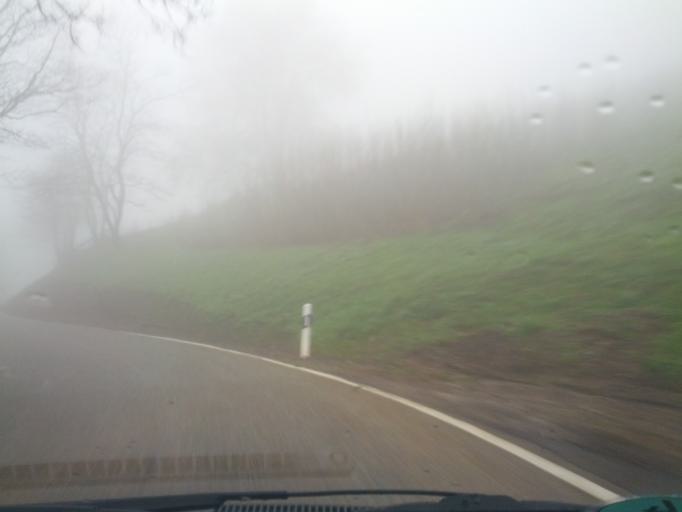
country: DE
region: Baden-Wuerttemberg
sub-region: Freiburg Region
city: Bollen
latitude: 47.8037
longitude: 7.8009
